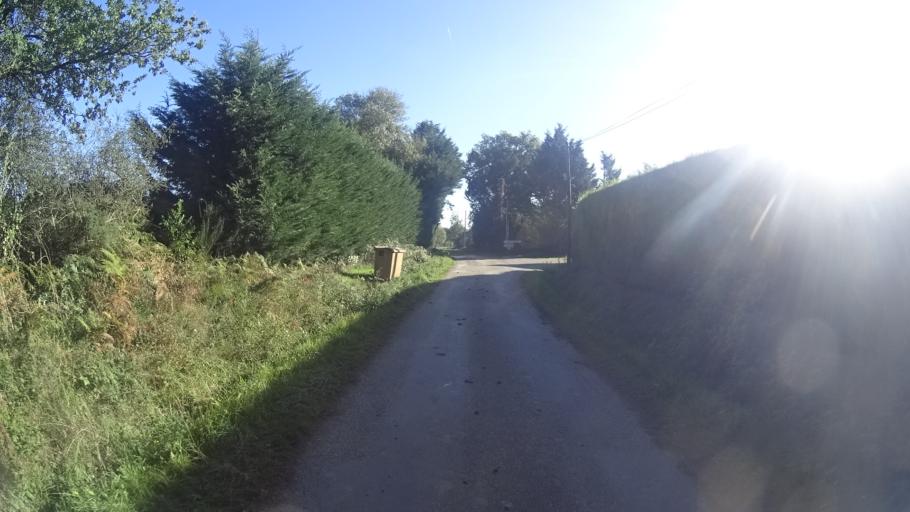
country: FR
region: Brittany
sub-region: Departement du Morbihan
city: Saint-Vincent-sur-Oust
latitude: 47.7081
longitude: -2.1720
